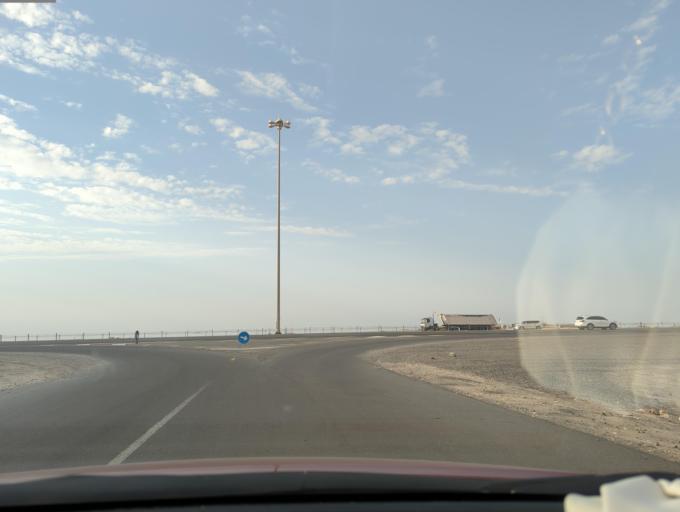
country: AE
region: Dubai
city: Dubai
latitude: 24.7273
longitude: 54.8737
